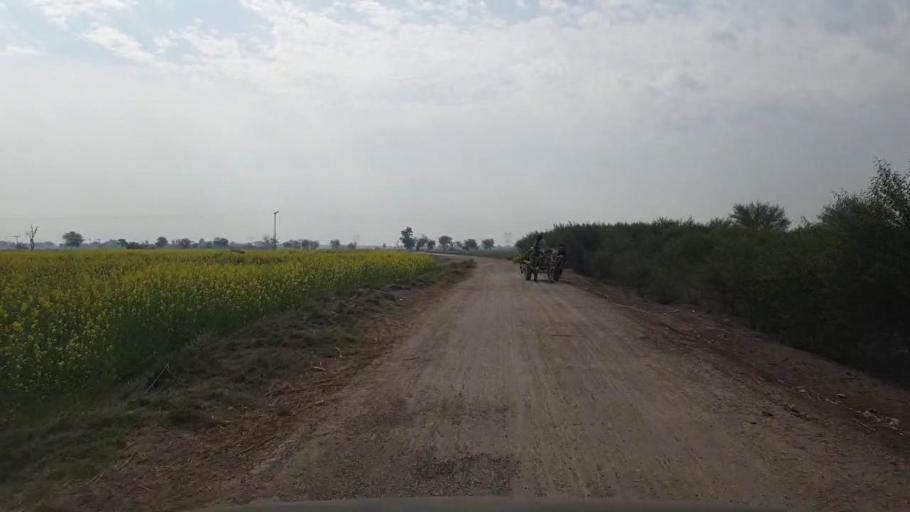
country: PK
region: Sindh
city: Hala
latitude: 25.9939
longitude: 68.4112
